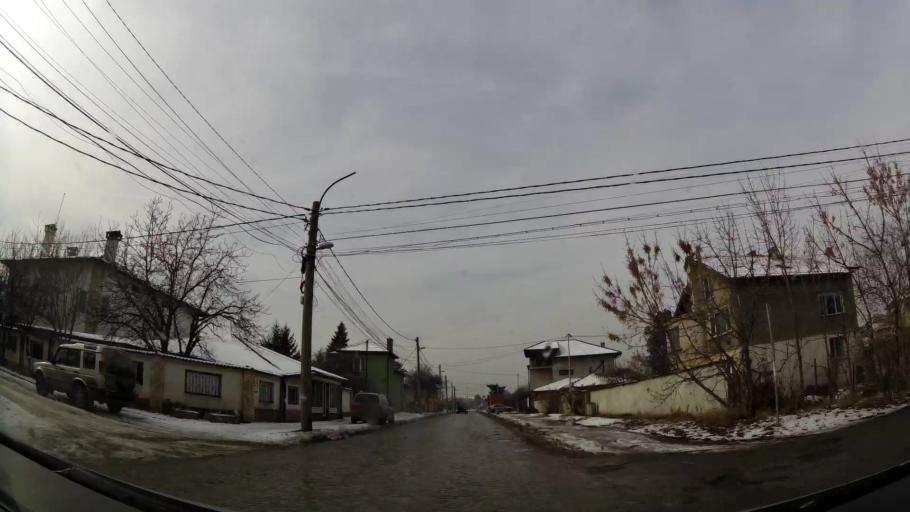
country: BG
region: Sofia-Capital
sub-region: Stolichna Obshtina
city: Sofia
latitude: 42.7124
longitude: 23.4108
